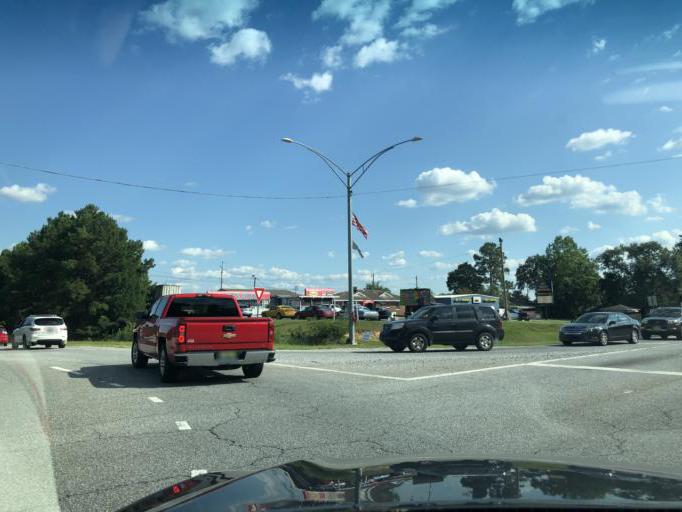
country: US
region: Georgia
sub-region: Muscogee County
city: Columbus
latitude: 32.5278
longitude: -84.9254
